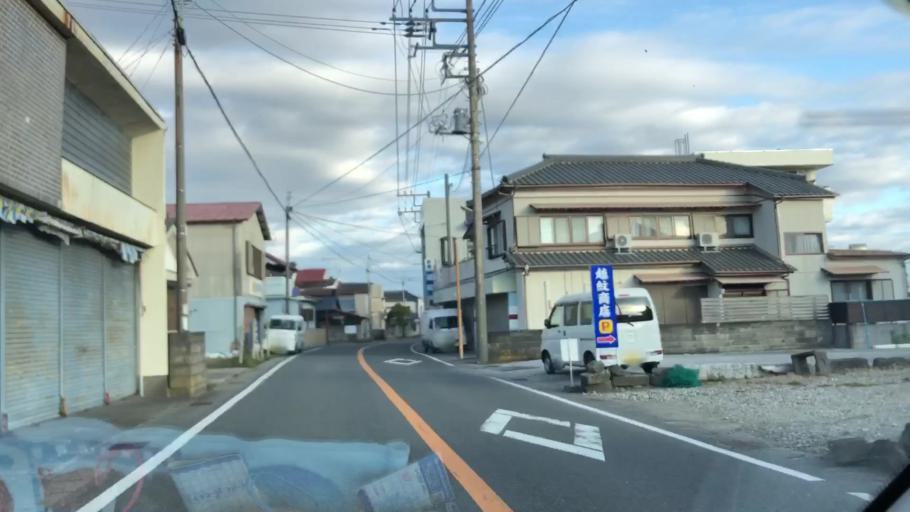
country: JP
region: Chiba
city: Tateyama
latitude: 34.9542
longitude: 139.9596
